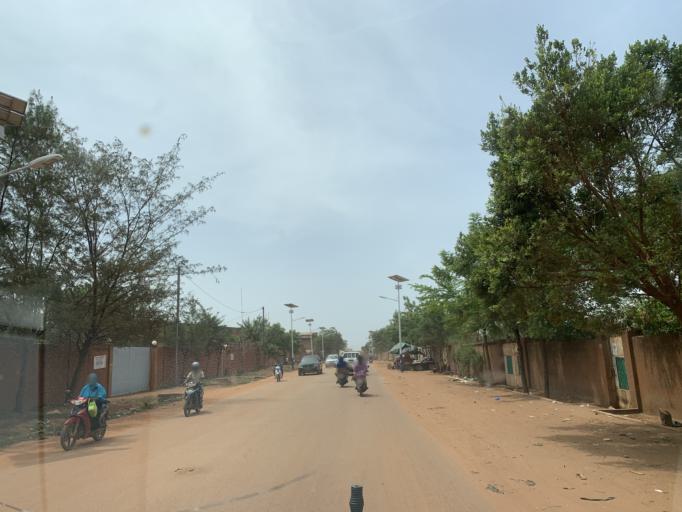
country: BF
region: Centre
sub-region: Kadiogo Province
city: Ouagadougou
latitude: 12.3349
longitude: -1.4971
